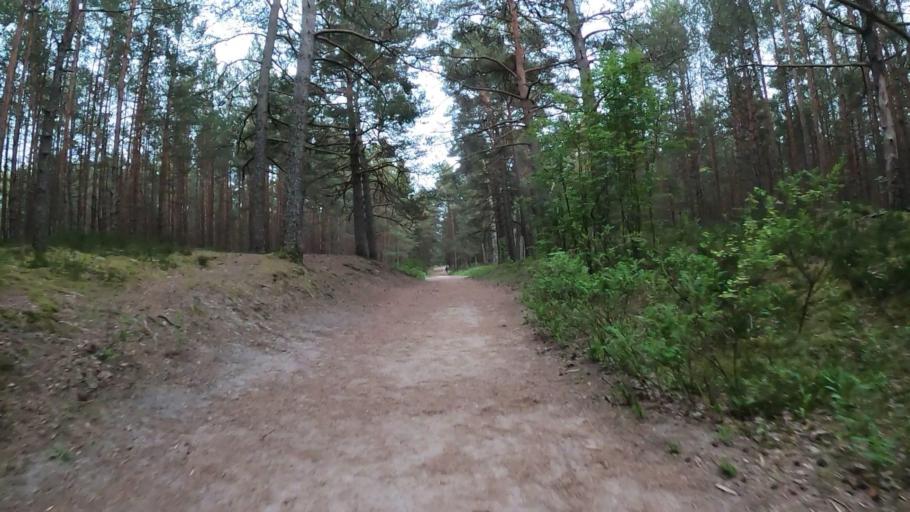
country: LV
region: Riga
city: Jaunciems
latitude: 57.0924
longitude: 24.1485
